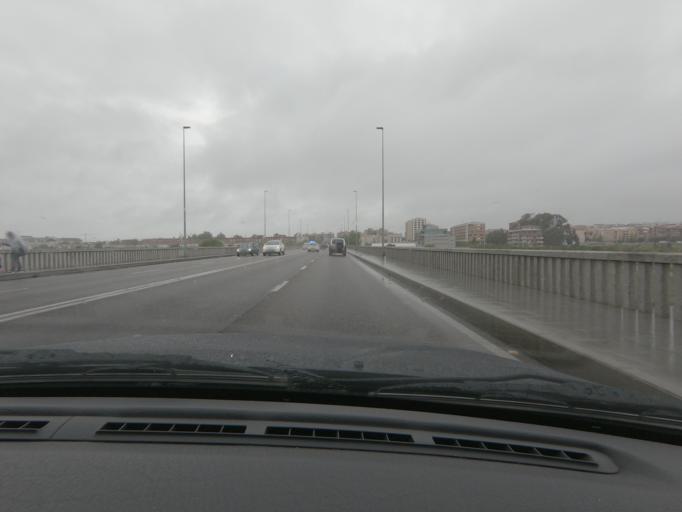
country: ES
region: Extremadura
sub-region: Provincia de Badajoz
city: Badajoz
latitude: 38.8805
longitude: -6.9824
